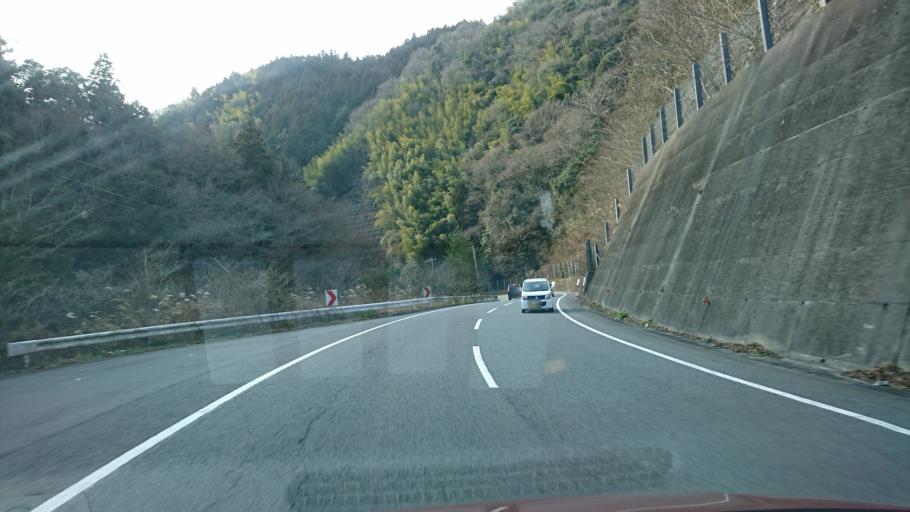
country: JP
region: Ehime
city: Hojo
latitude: 33.9144
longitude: 132.8818
